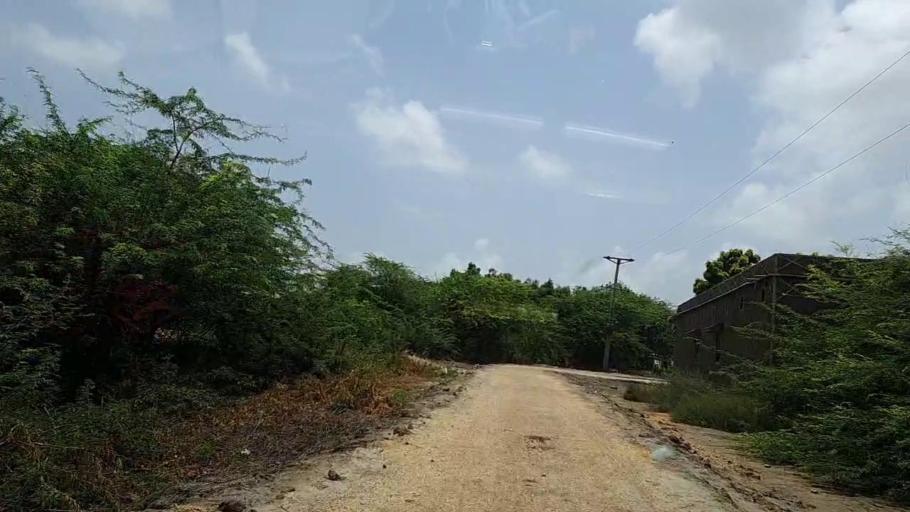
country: PK
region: Sindh
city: Keti Bandar
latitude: 24.1643
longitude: 67.5462
